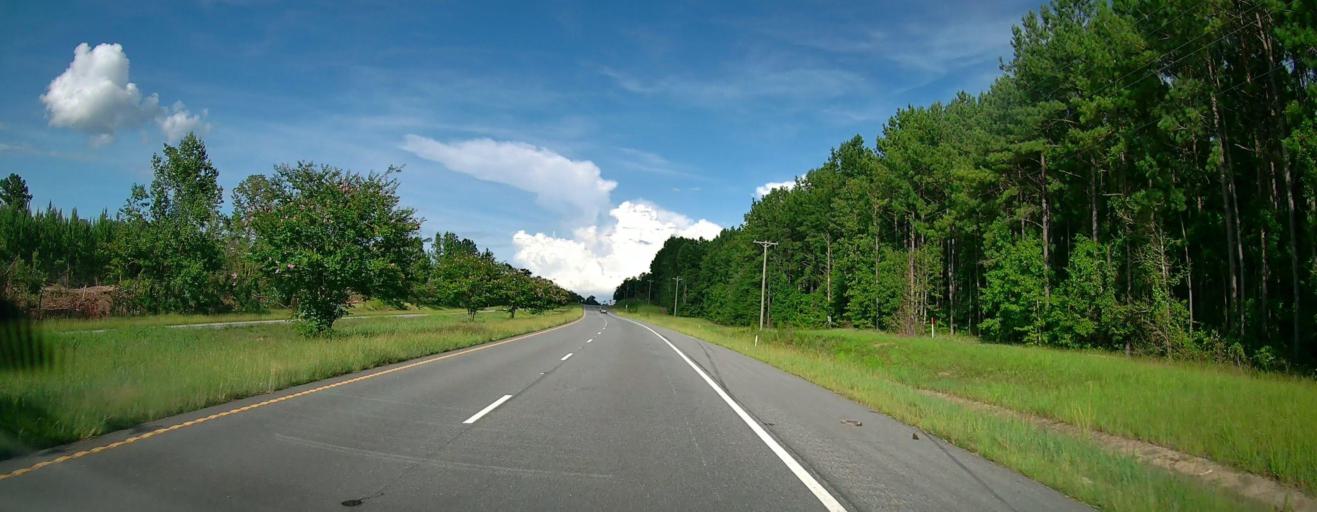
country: US
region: Georgia
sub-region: Talbot County
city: Talbotton
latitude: 32.5465
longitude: -84.7090
